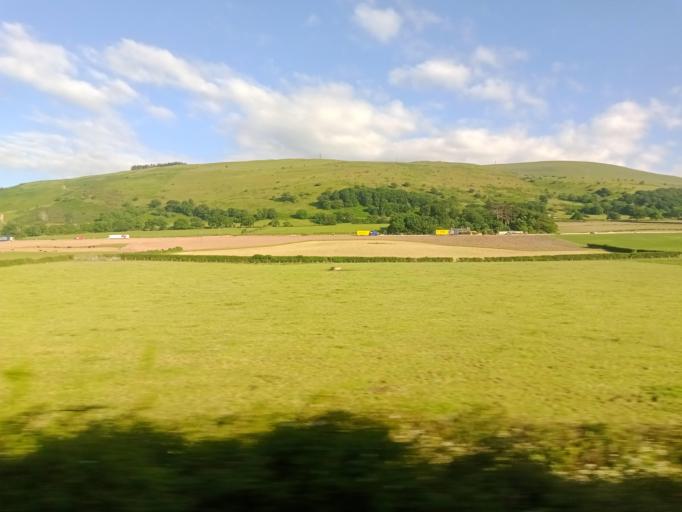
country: GB
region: Wales
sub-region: Gwynedd
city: Aber
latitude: 53.2350
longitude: -4.0322
